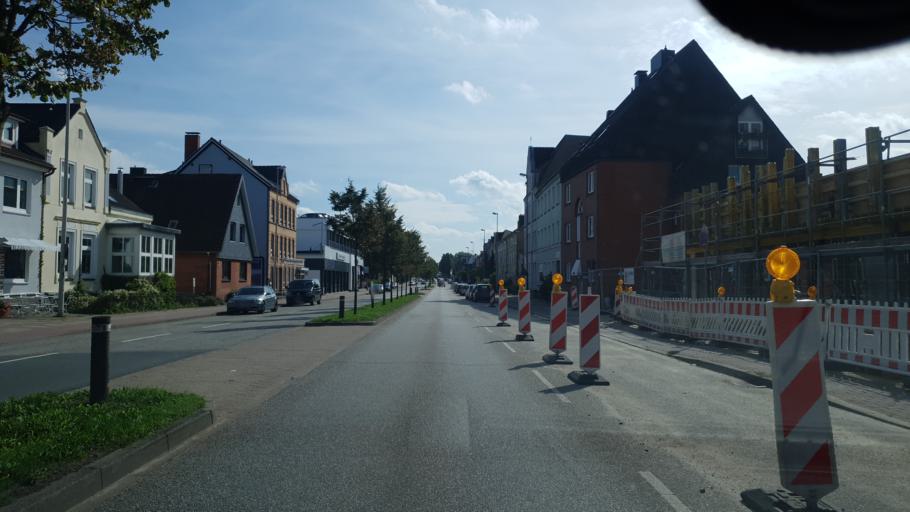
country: DE
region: Schleswig-Holstein
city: Kronshagen
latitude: 54.3431
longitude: 10.0996
